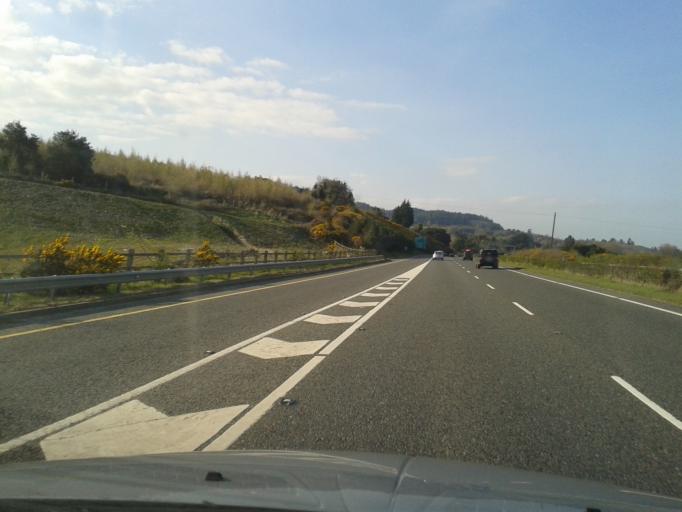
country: IE
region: Leinster
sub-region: Wicklow
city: Ashford
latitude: 53.0454
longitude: -6.0895
